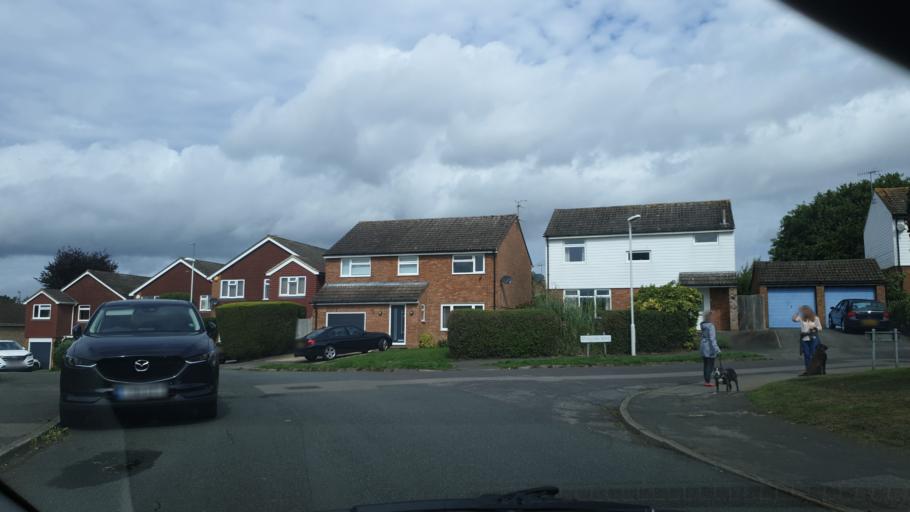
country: GB
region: England
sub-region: West Sussex
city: East Grinstead
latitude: 51.1362
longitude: 0.0088
